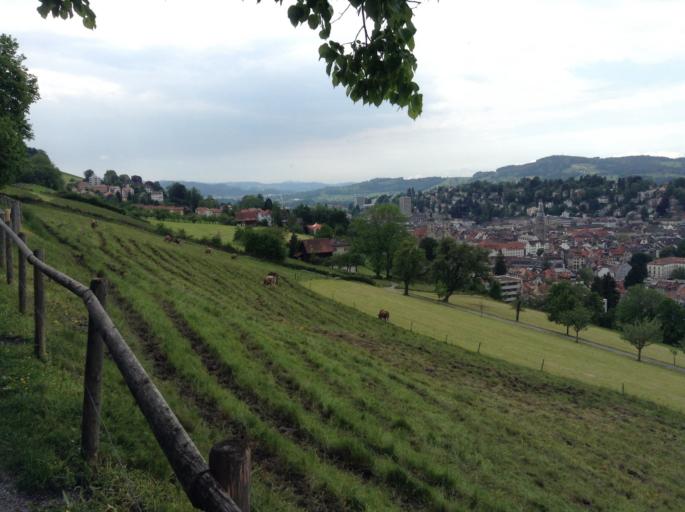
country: CH
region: Saint Gallen
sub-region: Wahlkreis St. Gallen
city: Sankt Gallen
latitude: 47.4228
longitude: 9.3888
